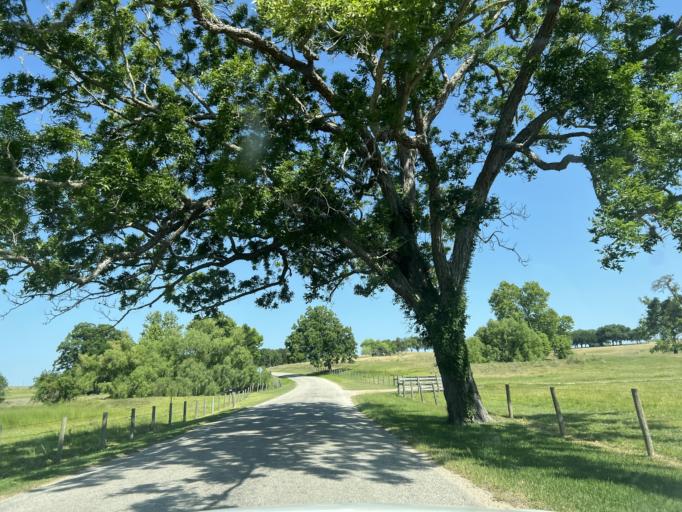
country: US
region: Texas
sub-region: Washington County
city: Brenham
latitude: 30.1720
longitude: -96.3392
